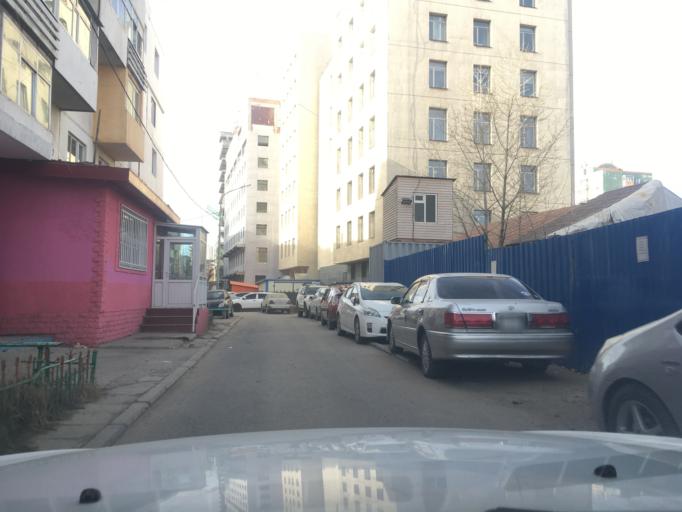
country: MN
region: Ulaanbaatar
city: Ulaanbaatar
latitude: 47.9141
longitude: 106.8808
